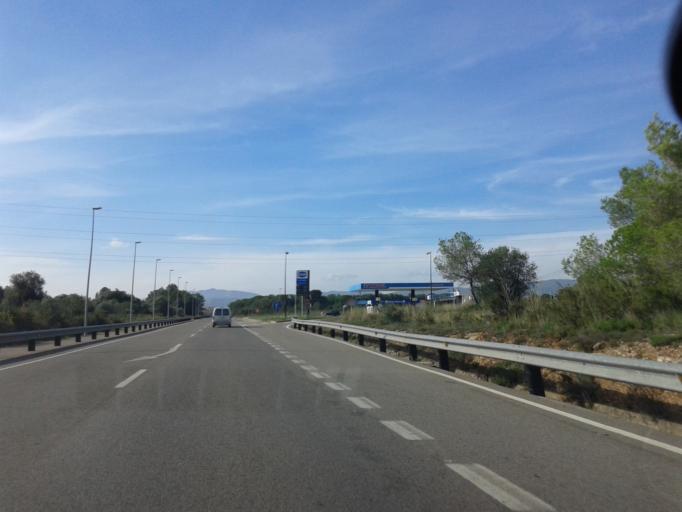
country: ES
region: Catalonia
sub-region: Provincia de Tarragona
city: Sant Jaume dels Domenys
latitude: 41.2748
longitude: 1.5936
